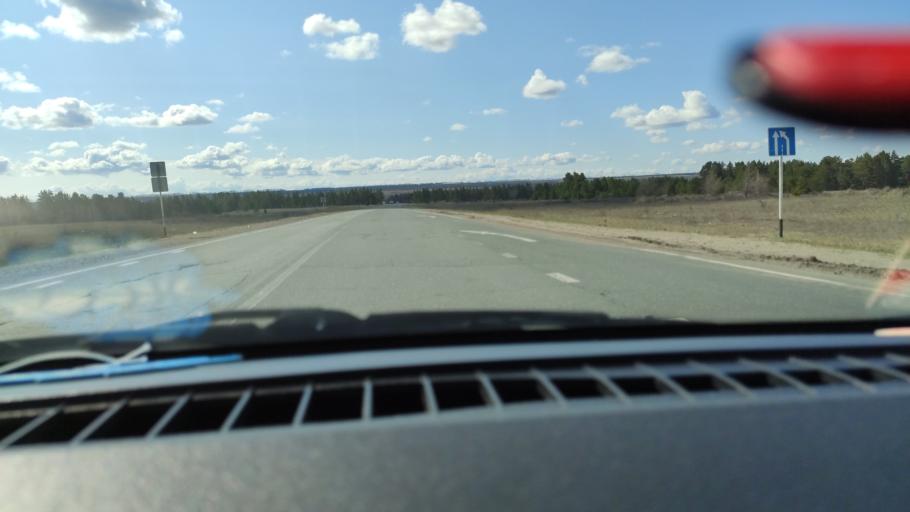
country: RU
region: Samara
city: Varlamovo
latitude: 53.1497
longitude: 48.2842
